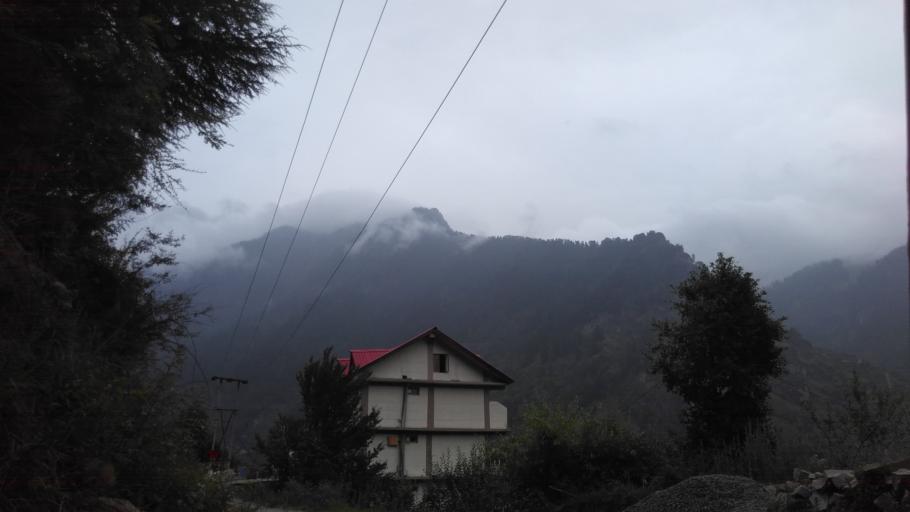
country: IN
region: Himachal Pradesh
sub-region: Kulu
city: Manali
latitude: 32.2249
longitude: 77.1846
